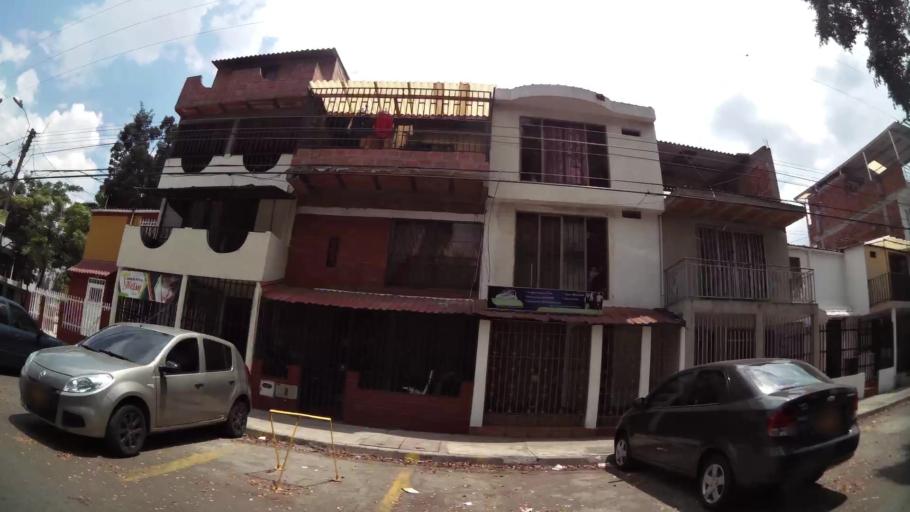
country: CO
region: Valle del Cauca
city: Cali
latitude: 3.4668
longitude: -76.4922
